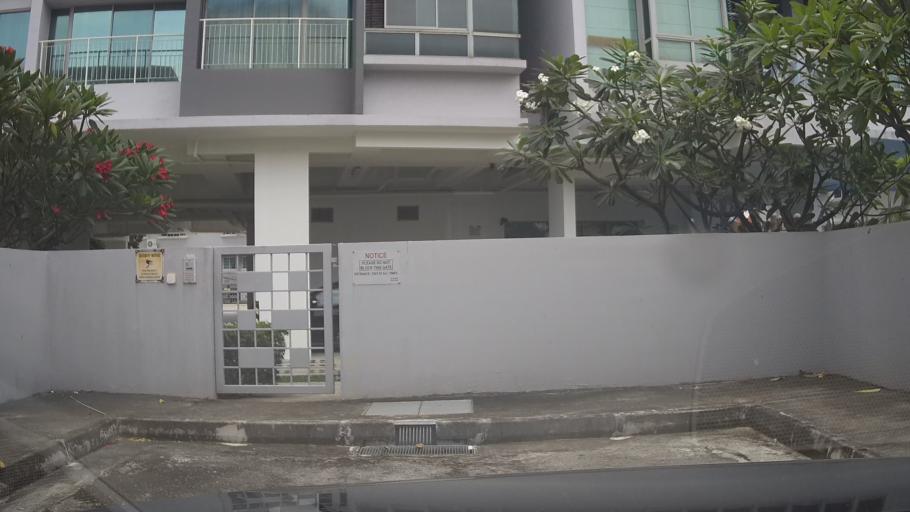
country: SG
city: Singapore
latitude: 1.3109
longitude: 103.9095
